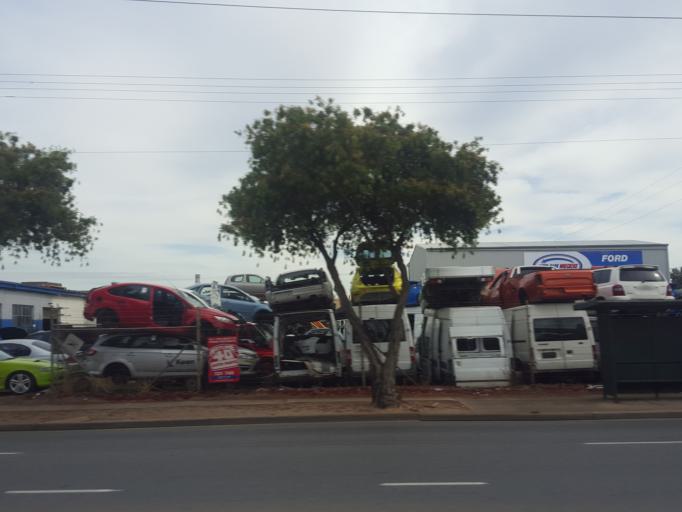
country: AU
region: South Australia
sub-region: Port Adelaide Enfield
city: Alberton
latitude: -34.8509
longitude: 138.5382
